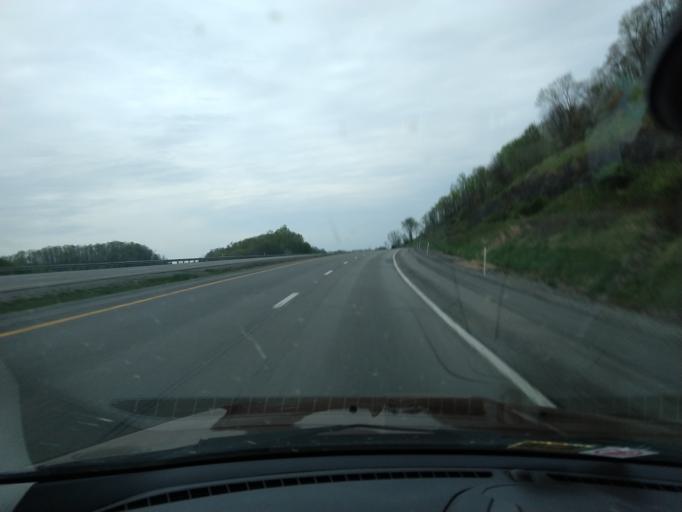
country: US
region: West Virginia
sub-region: Lewis County
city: Weston
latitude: 38.9271
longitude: -80.5465
